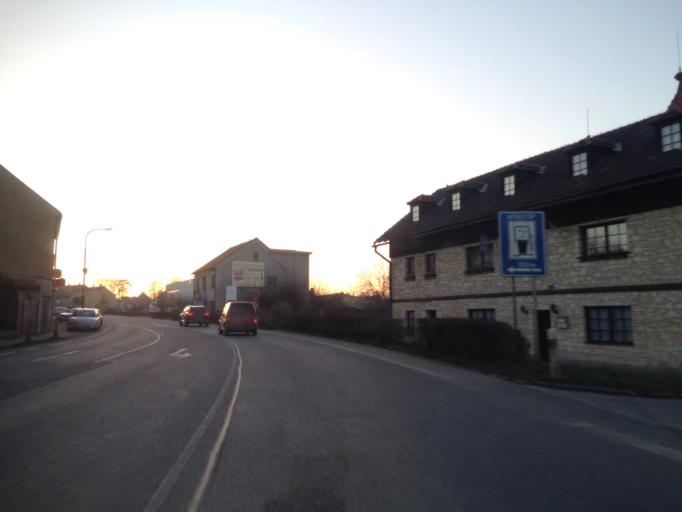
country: CZ
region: Central Bohemia
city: Revnicov
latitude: 50.1837
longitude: 13.8078
